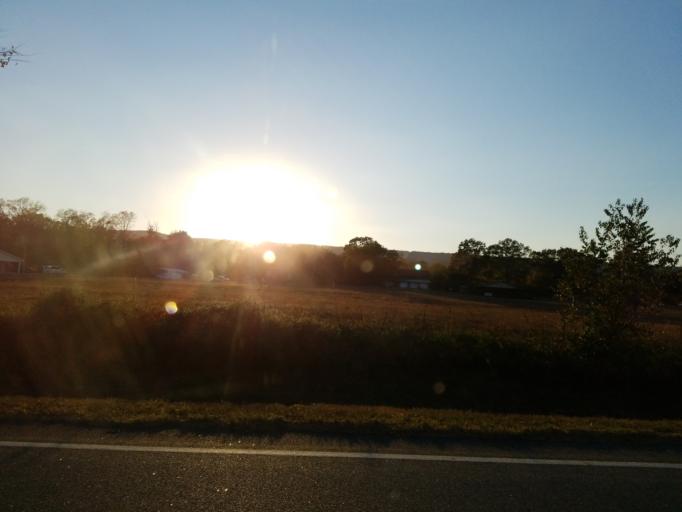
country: US
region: Georgia
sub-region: Gordon County
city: Calhoun
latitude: 34.5730
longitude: -85.0247
